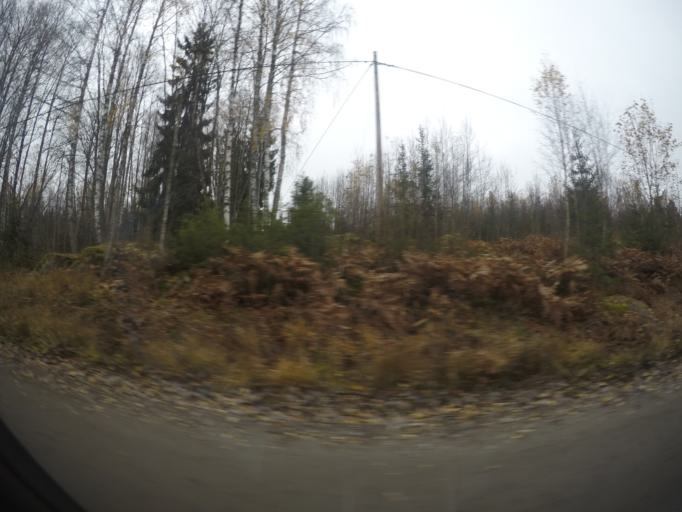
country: SE
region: Vaestmanland
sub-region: Surahammars Kommun
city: Ramnas
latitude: 59.7183
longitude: 16.0926
